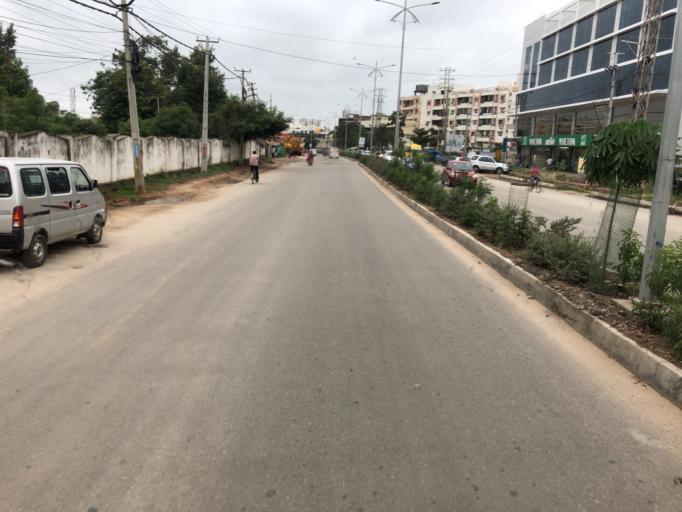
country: IN
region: Telangana
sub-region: Medak
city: Serilingampalle
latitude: 17.4641
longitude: 78.3456
